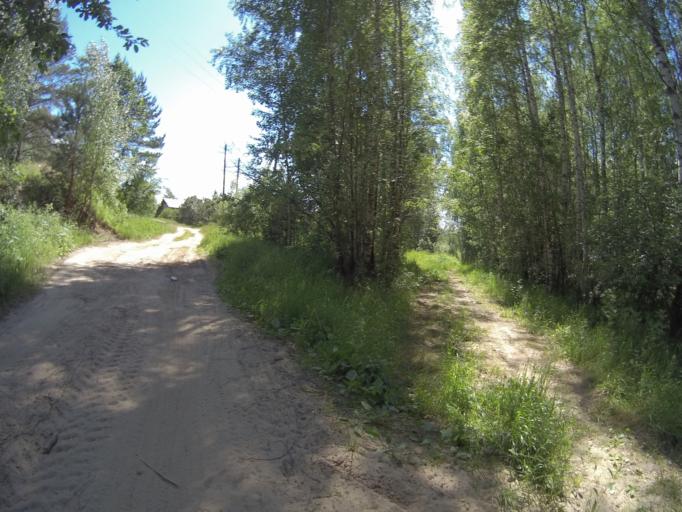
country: RU
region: Vladimir
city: Golovino
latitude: 56.0003
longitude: 40.4261
